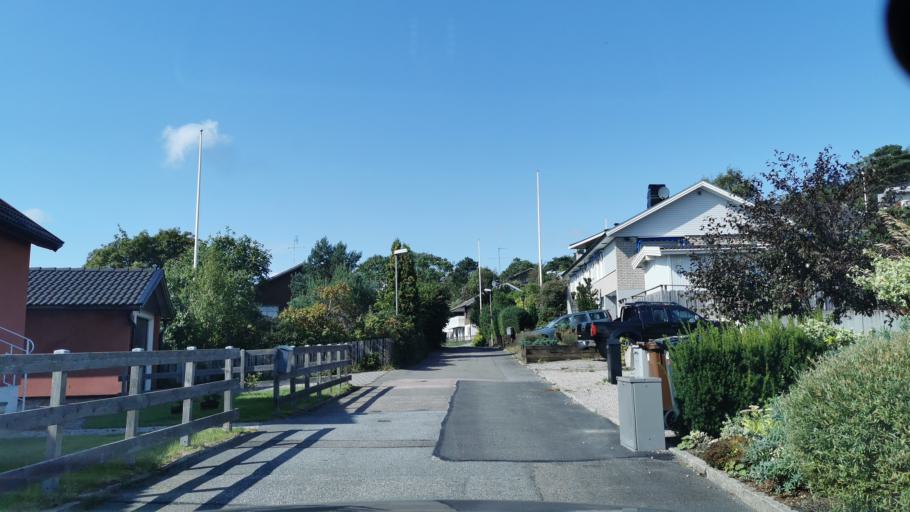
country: SE
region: Vaestra Goetaland
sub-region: Goteborg
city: Majorna
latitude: 57.6383
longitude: 11.9081
